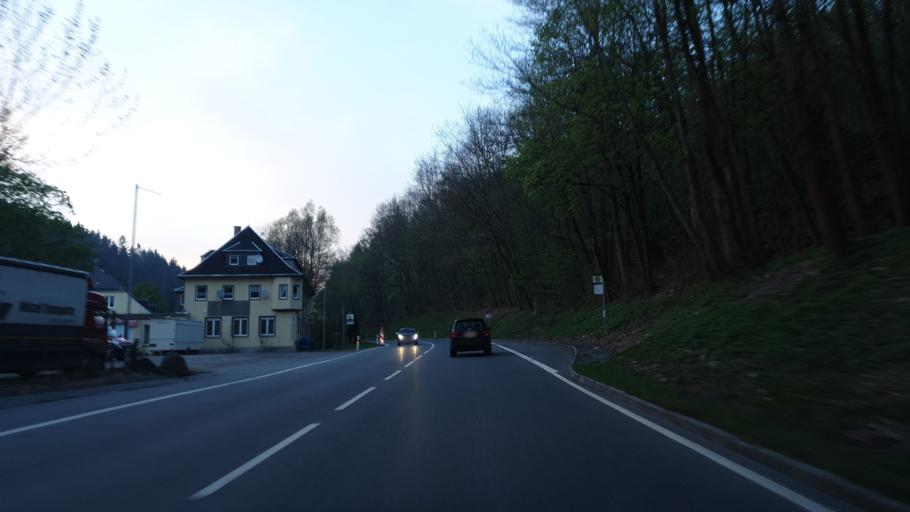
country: DE
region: Saxony
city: Aue
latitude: 50.6024
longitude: 12.7178
